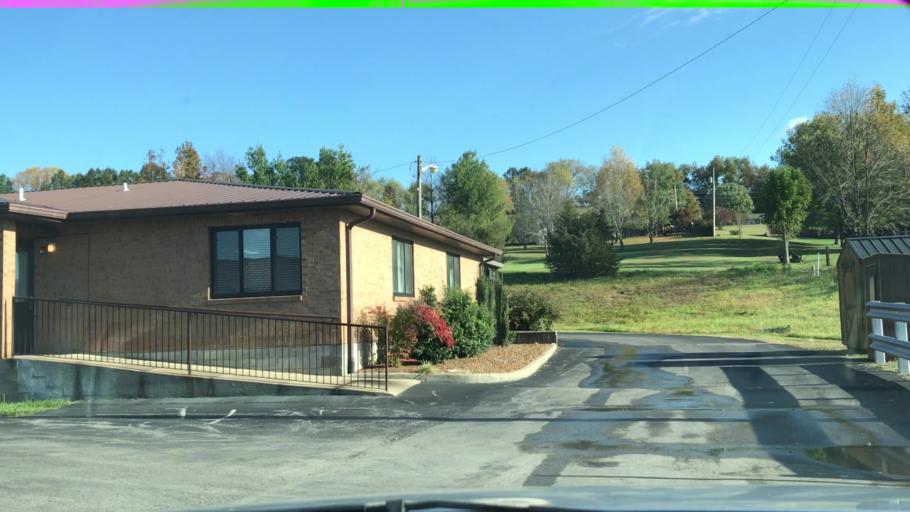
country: US
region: Kentucky
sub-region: Metcalfe County
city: Edmonton
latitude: 36.9879
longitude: -85.6319
